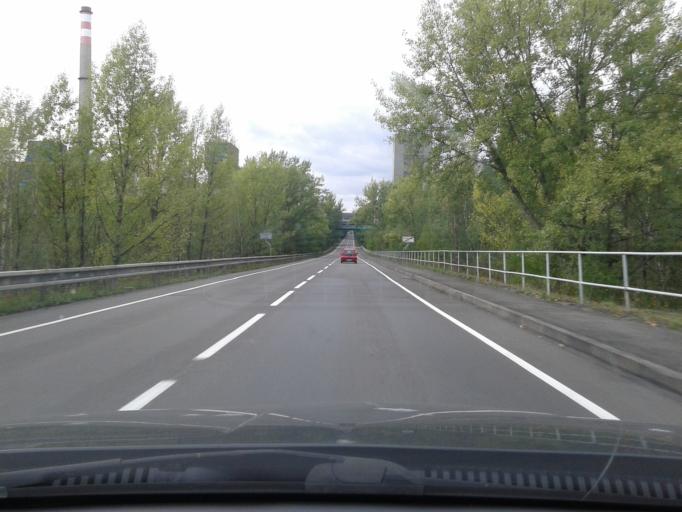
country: CZ
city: Doubrava
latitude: 49.8440
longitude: 18.5018
